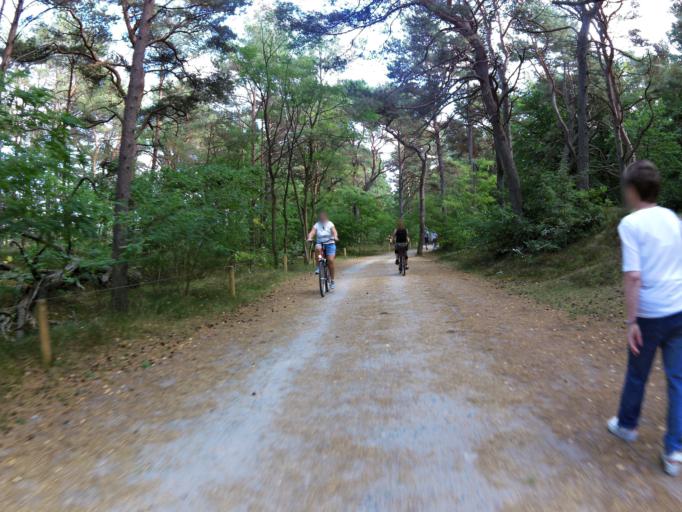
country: DE
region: Mecklenburg-Vorpommern
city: Ostseebad Zinnowitz
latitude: 54.0866
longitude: 13.9007
